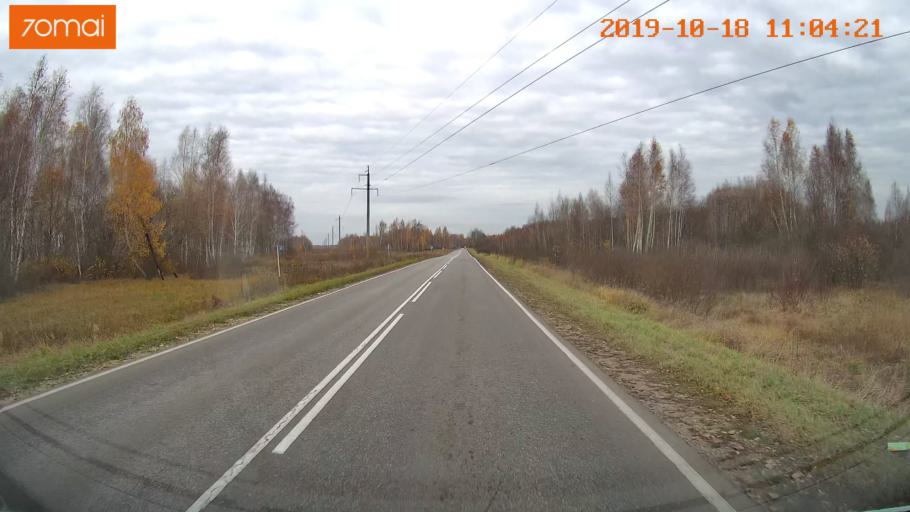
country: RU
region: Tula
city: Yepifan'
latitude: 53.8926
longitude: 38.5491
